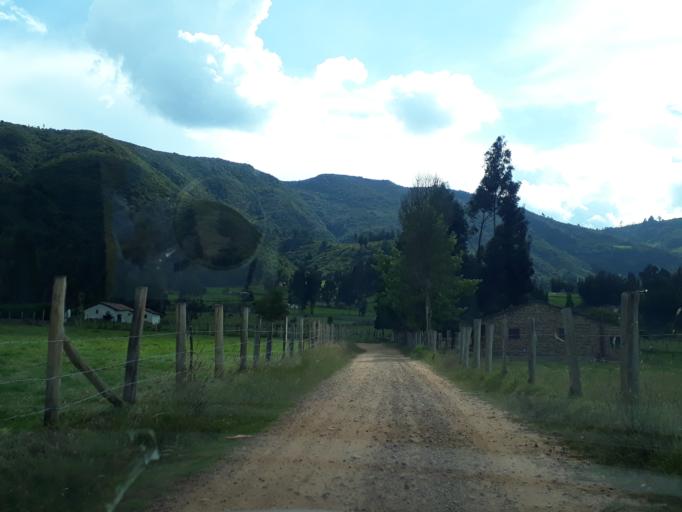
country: CO
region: Boyaca
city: Santa Rosa de Viterbo
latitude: 5.8503
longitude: -72.9558
